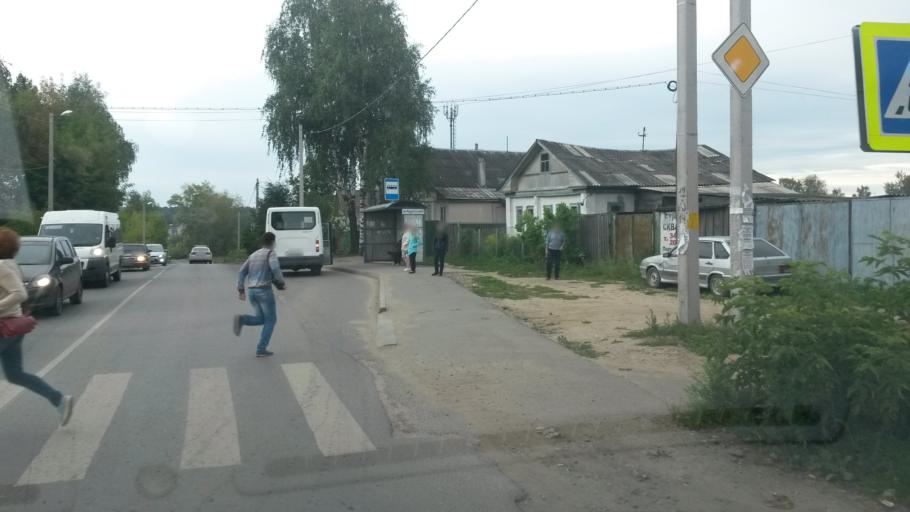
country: RU
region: Ivanovo
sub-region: Gorod Ivanovo
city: Ivanovo
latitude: 57.0303
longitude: 40.9233
